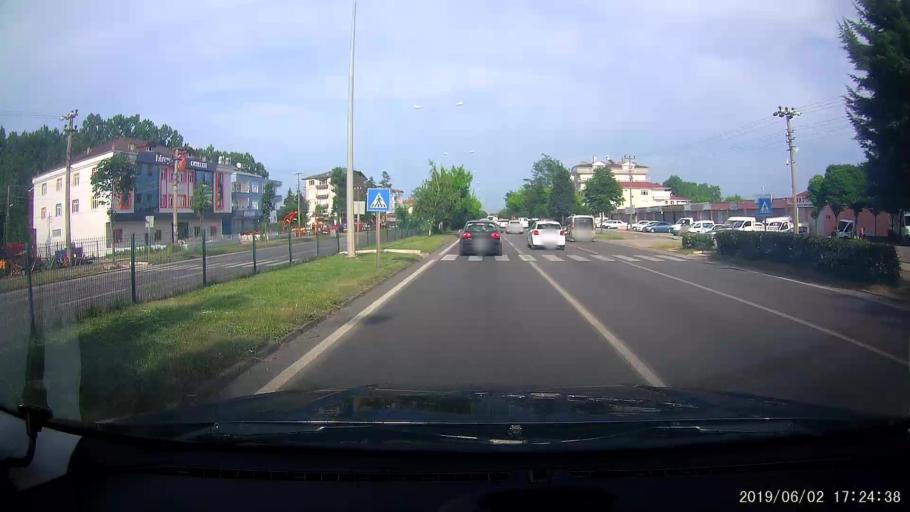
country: TR
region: Samsun
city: Carsamba
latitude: 41.2053
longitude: 36.7046
